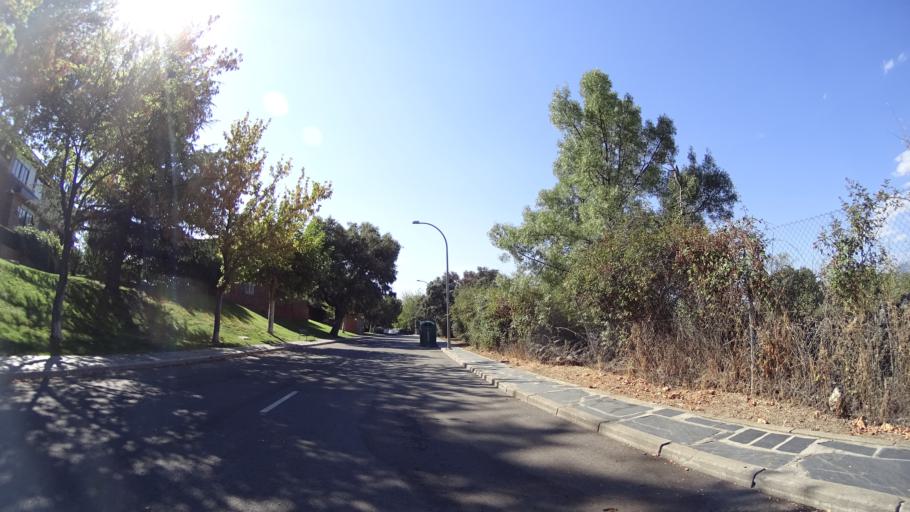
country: ES
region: Madrid
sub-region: Provincia de Madrid
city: Navalquejigo
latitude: 40.6090
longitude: -4.0325
